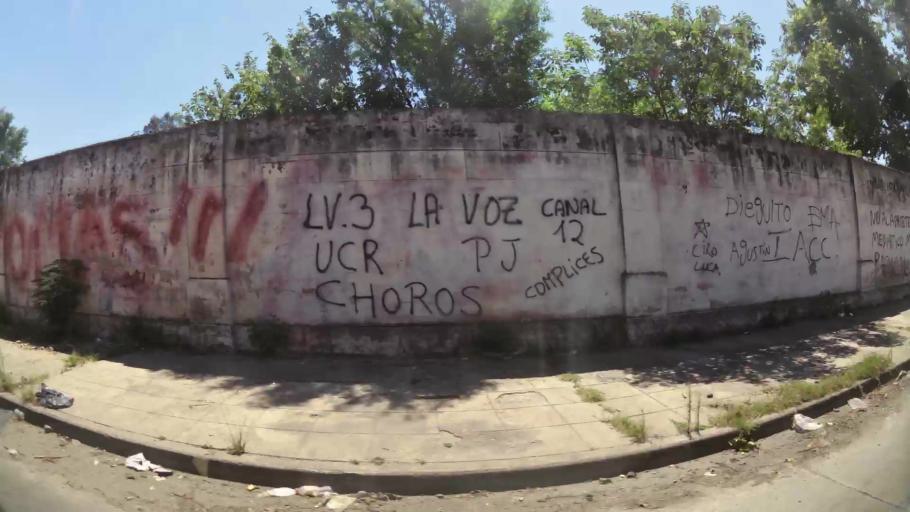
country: AR
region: Cordoba
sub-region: Departamento de Capital
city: Cordoba
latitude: -31.3886
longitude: -64.1923
